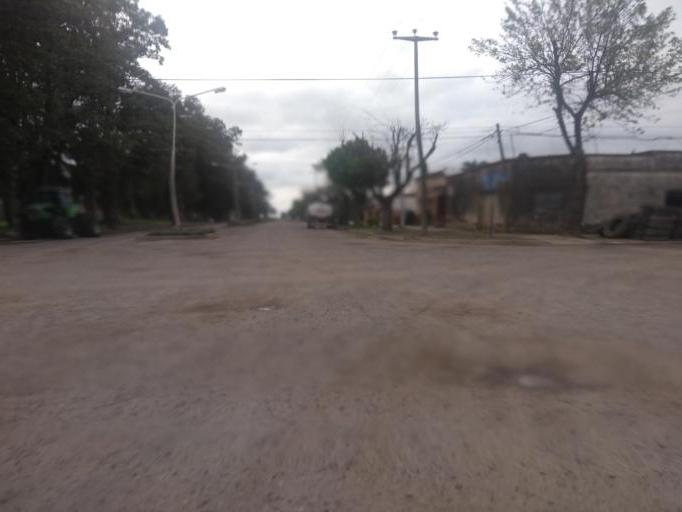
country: AR
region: Santa Fe
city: Galvez
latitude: -31.9072
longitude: -61.2800
